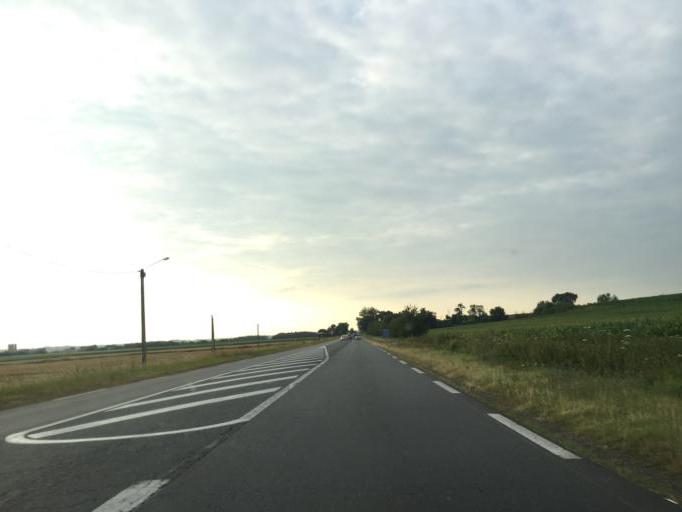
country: FR
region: Auvergne
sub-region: Departement de l'Allier
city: Varennes-sur-Allier
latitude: 46.3611
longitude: 3.3708
